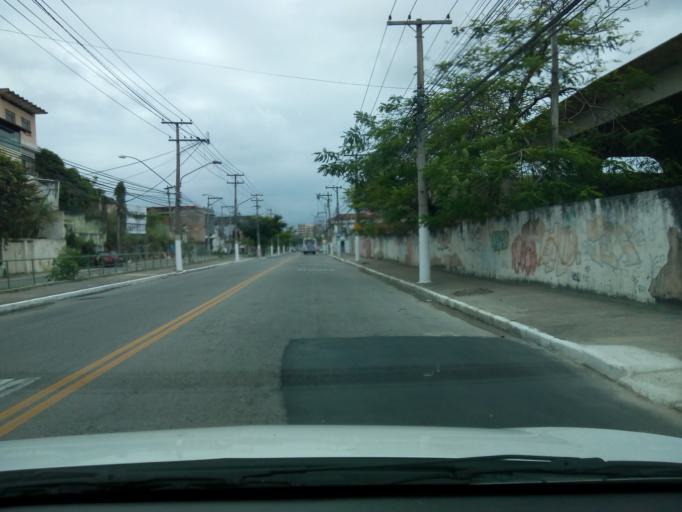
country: BR
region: Rio de Janeiro
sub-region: Niteroi
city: Niteroi
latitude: -22.8681
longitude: -43.1041
